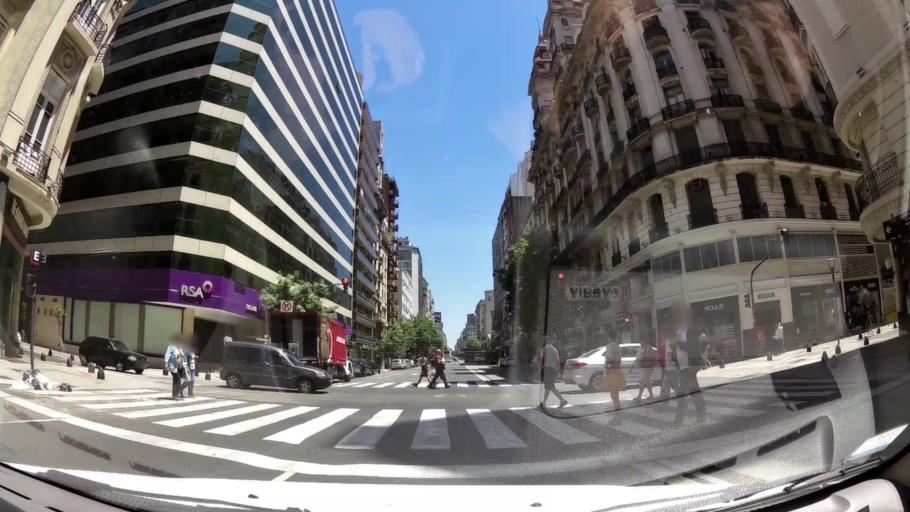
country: AR
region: Buenos Aires F.D.
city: Buenos Aires
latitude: -34.5990
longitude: -58.3782
